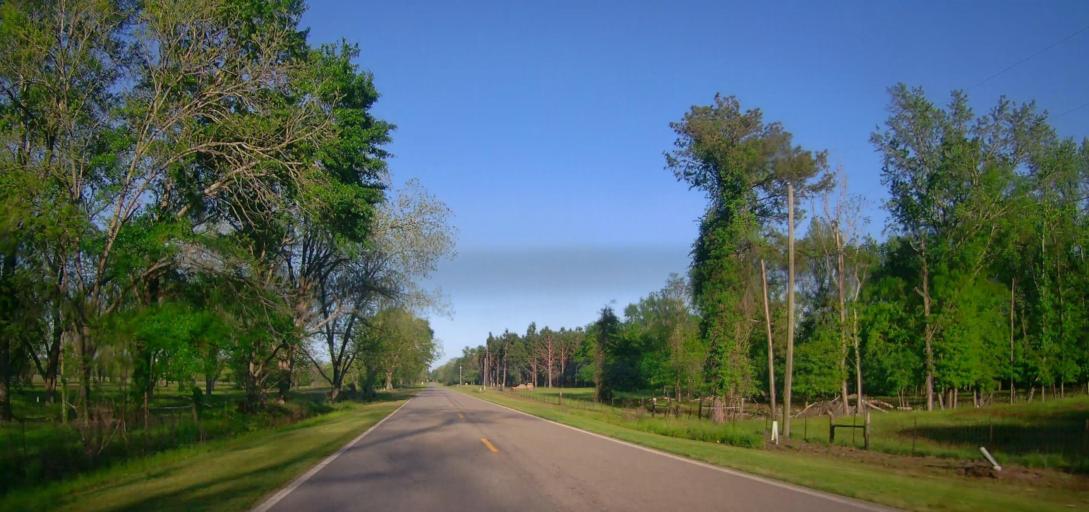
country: US
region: Georgia
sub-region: Macon County
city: Oglethorpe
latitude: 32.3016
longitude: -84.0804
